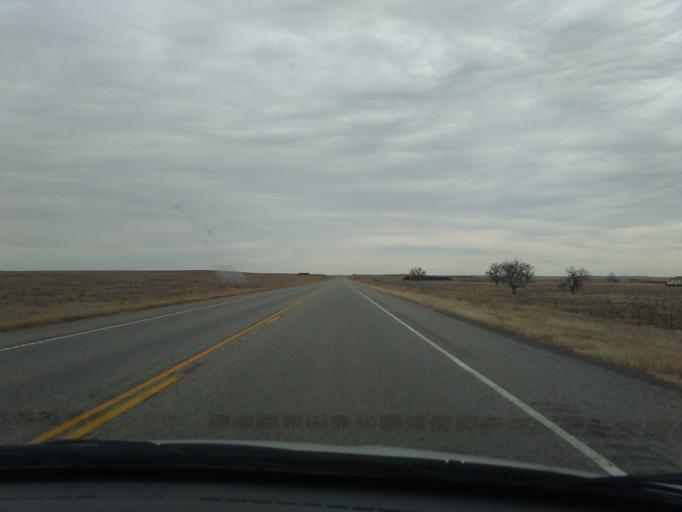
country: US
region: Colorado
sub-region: Washington County
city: Akron
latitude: 40.2249
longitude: -103.3930
